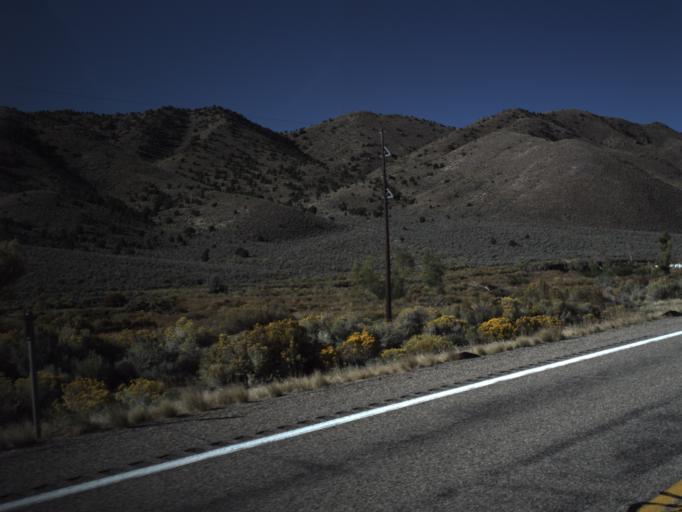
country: US
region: Utah
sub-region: Beaver County
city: Milford
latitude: 38.2140
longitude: -112.8757
